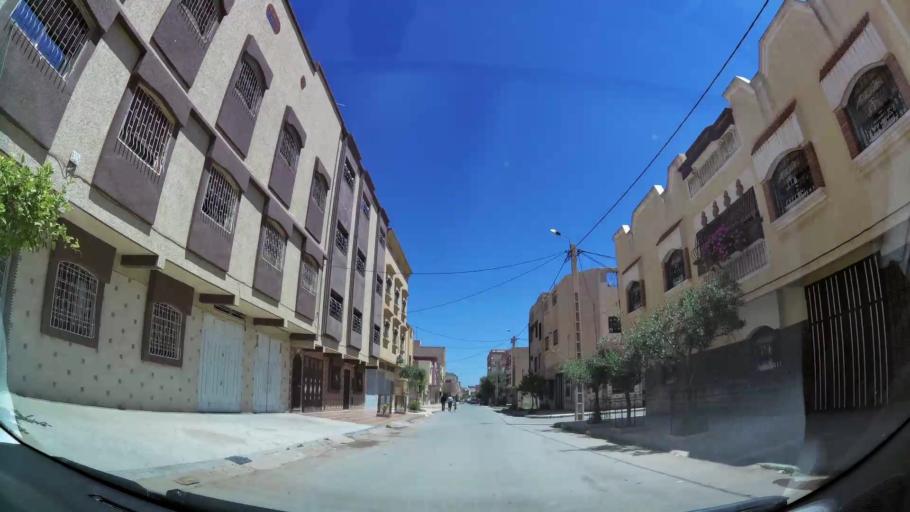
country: MA
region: Oriental
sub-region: Oujda-Angad
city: Oujda
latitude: 34.6724
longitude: -1.8918
